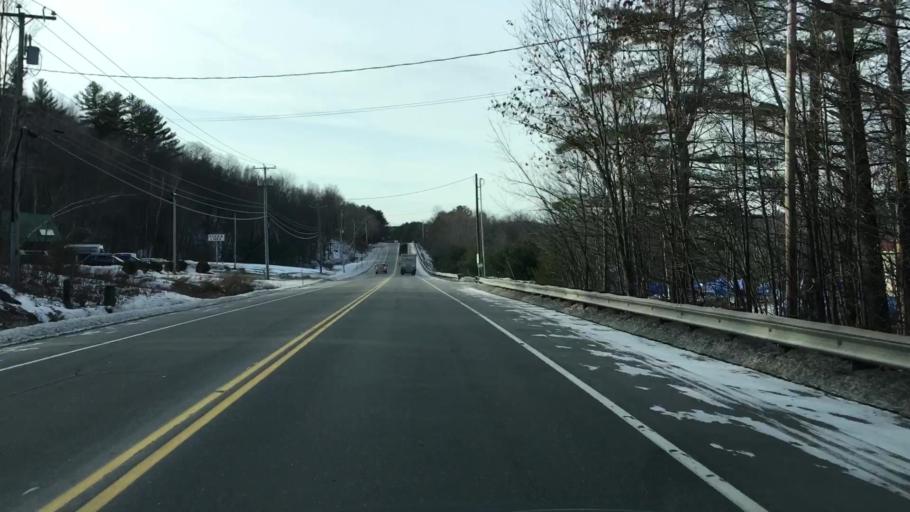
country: US
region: New Hampshire
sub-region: Sullivan County
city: Sunapee
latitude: 43.3855
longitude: -72.0913
